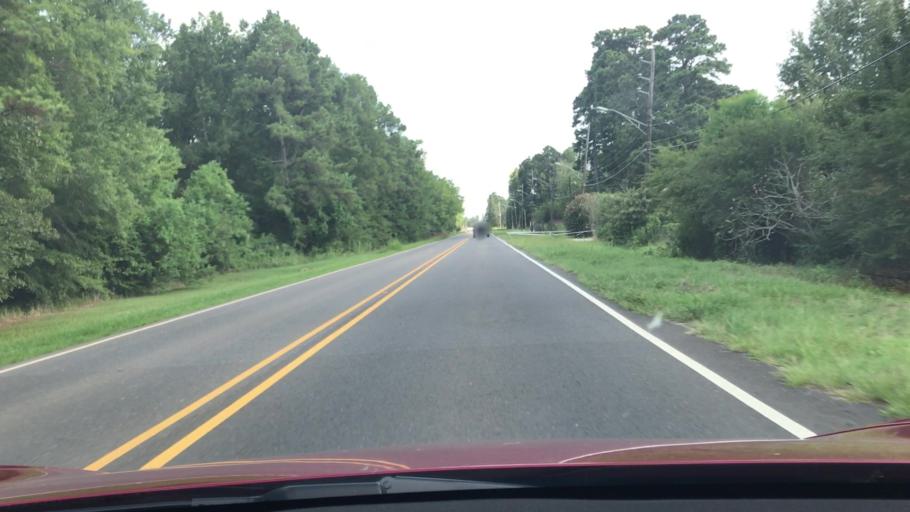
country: US
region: Louisiana
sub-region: Bossier Parish
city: Bossier City
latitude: 32.3952
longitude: -93.7386
